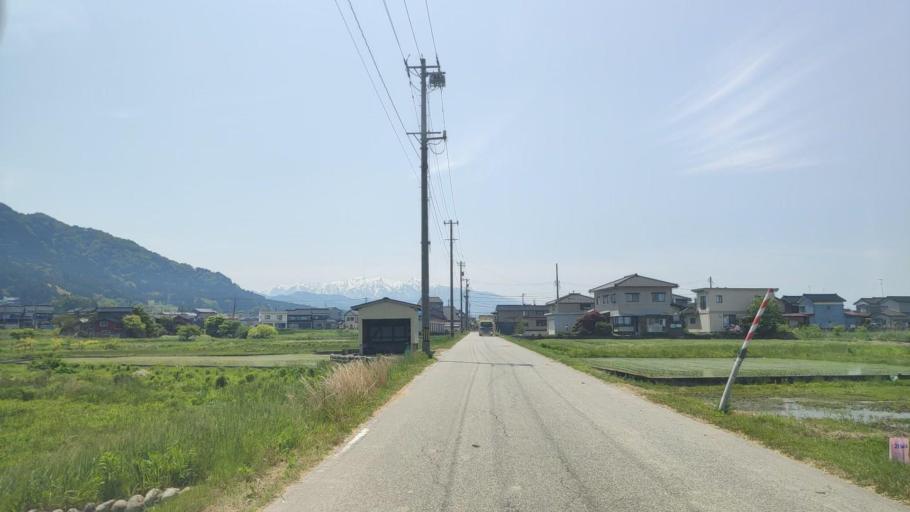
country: JP
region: Toyama
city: Nyuzen
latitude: 36.9598
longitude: 137.5681
